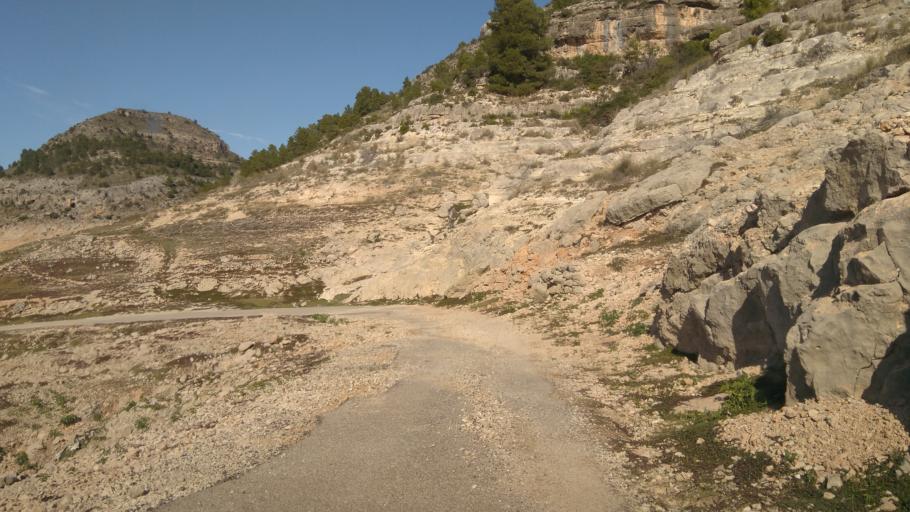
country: ES
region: Valencia
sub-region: Provincia de Valencia
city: Sumacarcer
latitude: 39.1536
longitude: -0.6569
